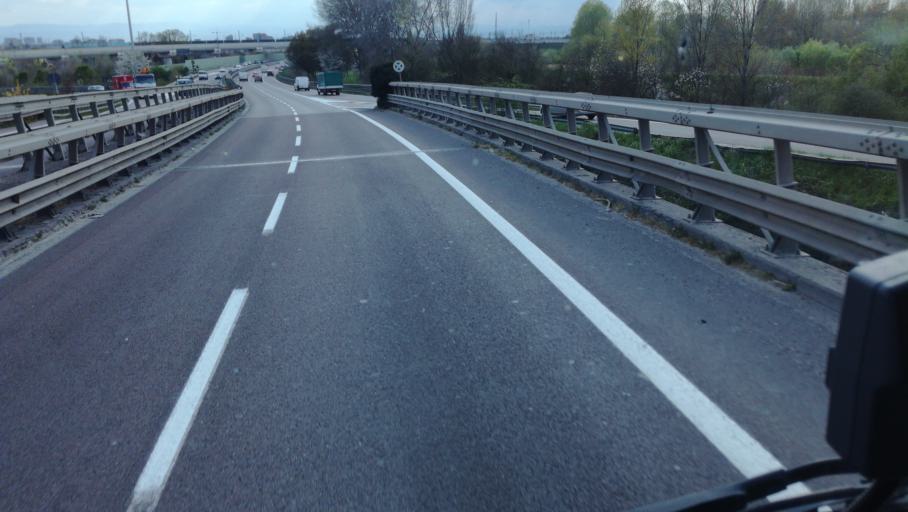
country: IT
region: Emilia-Romagna
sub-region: Provincia di Modena
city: Villanova
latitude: 44.6706
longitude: 10.9092
